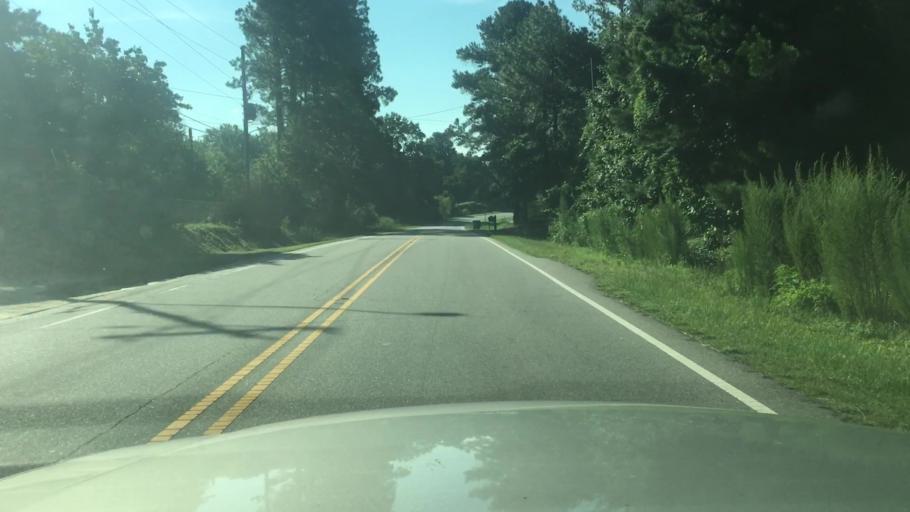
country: US
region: North Carolina
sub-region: Cumberland County
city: Fayetteville
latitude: 35.1268
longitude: -78.8905
